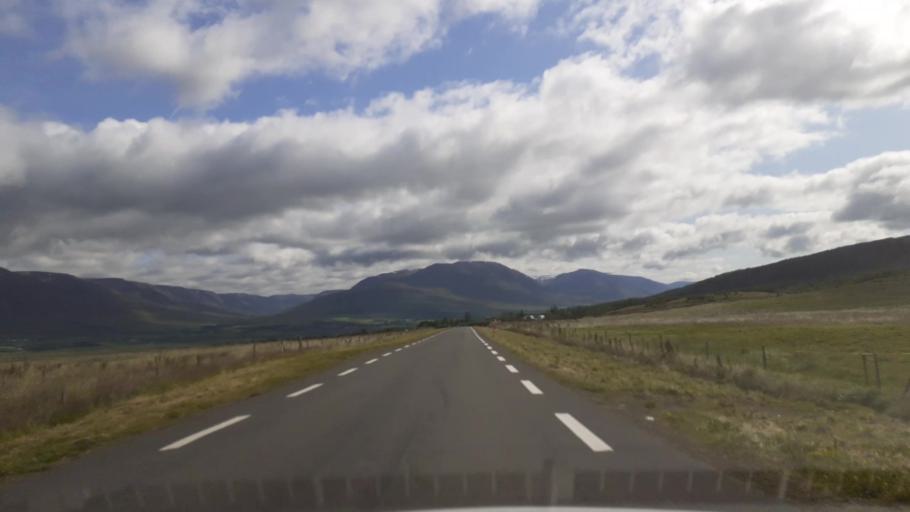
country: IS
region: Northeast
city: Akureyri
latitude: 65.6547
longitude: -18.0956
